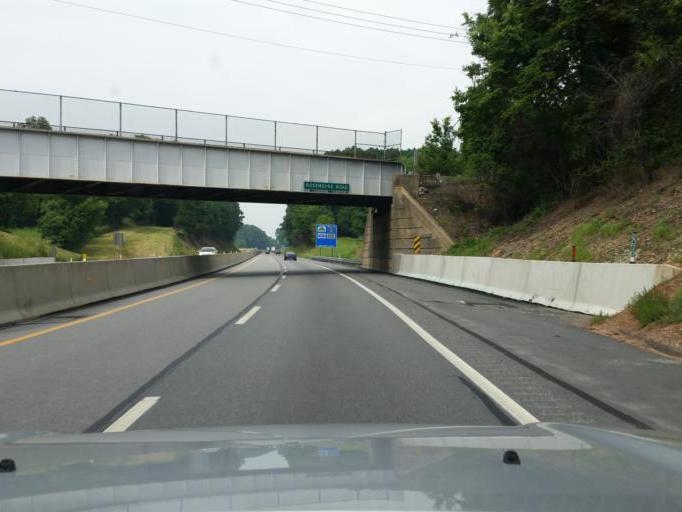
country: US
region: Pennsylvania
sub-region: Cumberland County
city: Shiremanstown
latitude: 40.1999
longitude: -76.9490
